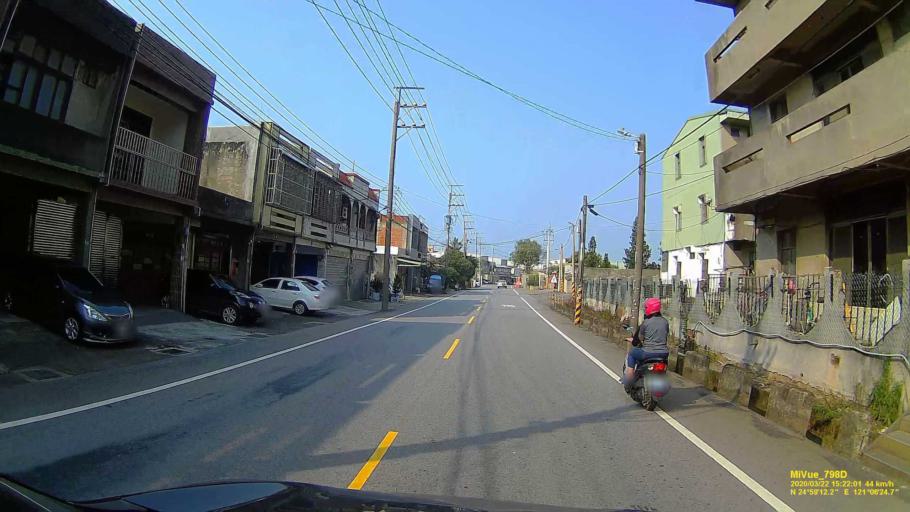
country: TW
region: Taiwan
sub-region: Hsinchu
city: Zhubei
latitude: 24.9867
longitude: 121.1069
